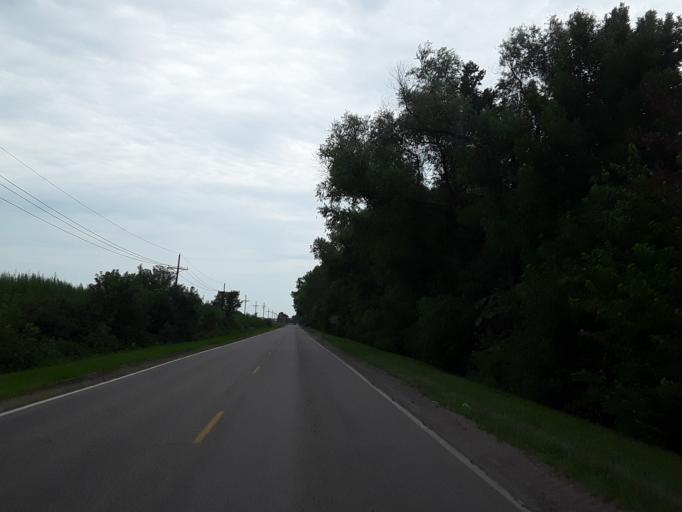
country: US
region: Nebraska
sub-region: Saunders County
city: Yutan
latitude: 41.2299
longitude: -96.3303
